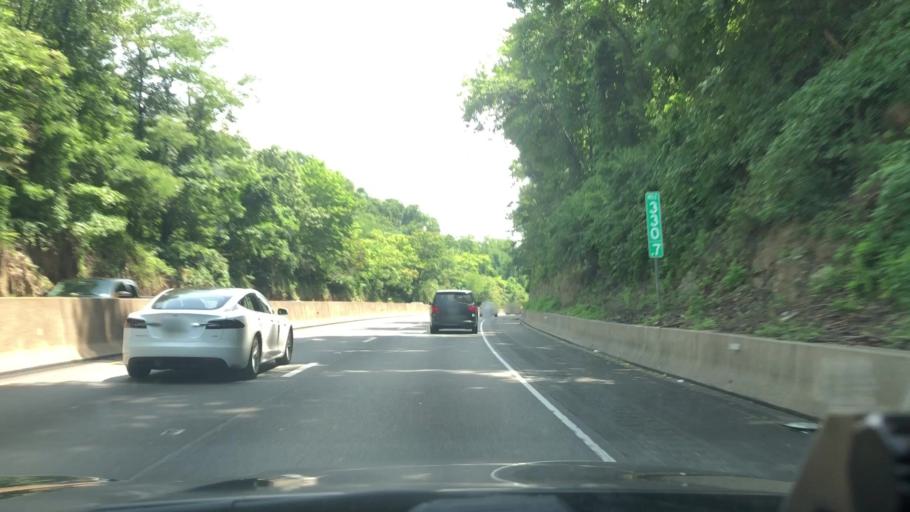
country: US
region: Pennsylvania
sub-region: Montgomery County
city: West Conshohocken
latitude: 40.0671
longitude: -75.3355
